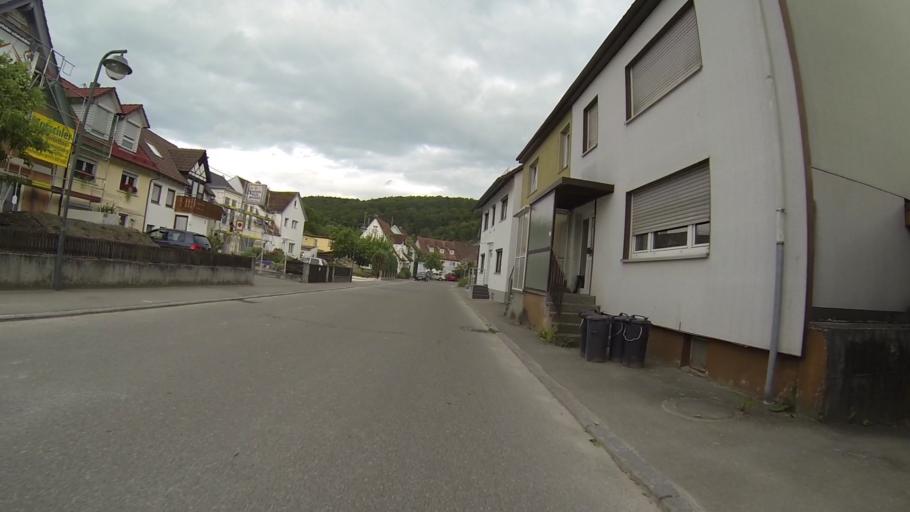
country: DE
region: Baden-Wuerttemberg
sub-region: Tuebingen Region
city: Blaubeuren
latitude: 48.3978
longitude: 9.8028
